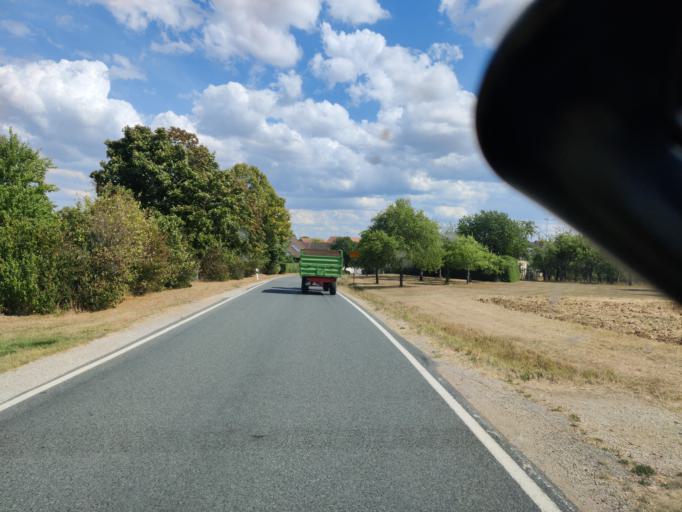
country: DE
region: Bavaria
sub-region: Regierungsbezirk Mittelfranken
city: Thalmassing
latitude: 49.0706
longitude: 11.2210
